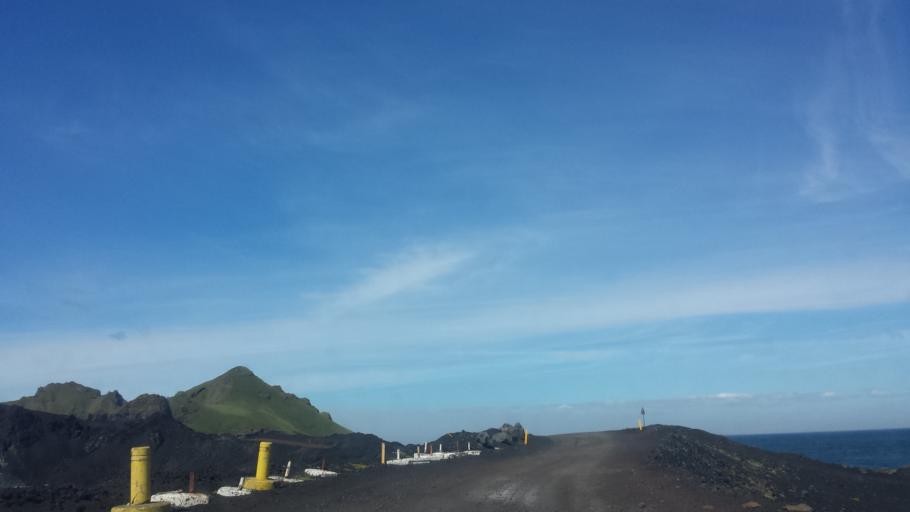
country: IS
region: South
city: Vestmannaeyjar
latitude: 63.4375
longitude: -20.2300
